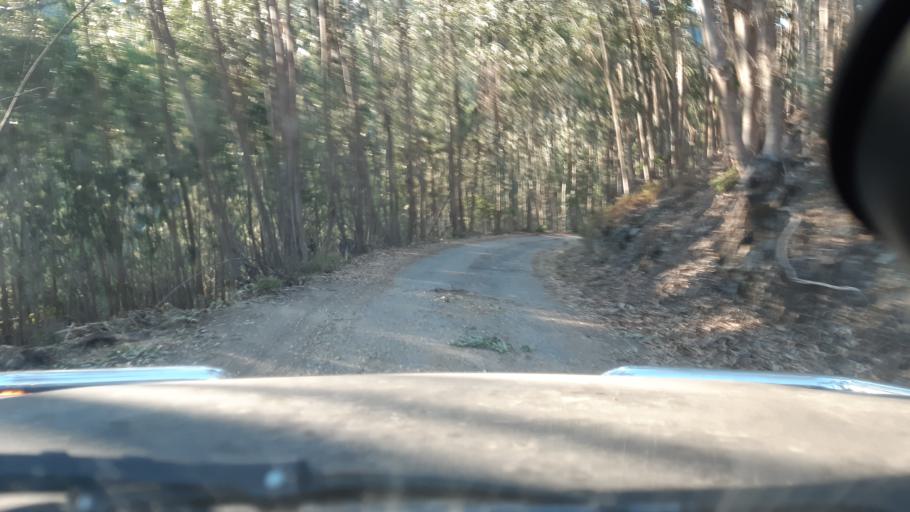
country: PT
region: Viseu
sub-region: Mortagua
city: Mortagua
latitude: 40.5269
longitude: -8.2557
